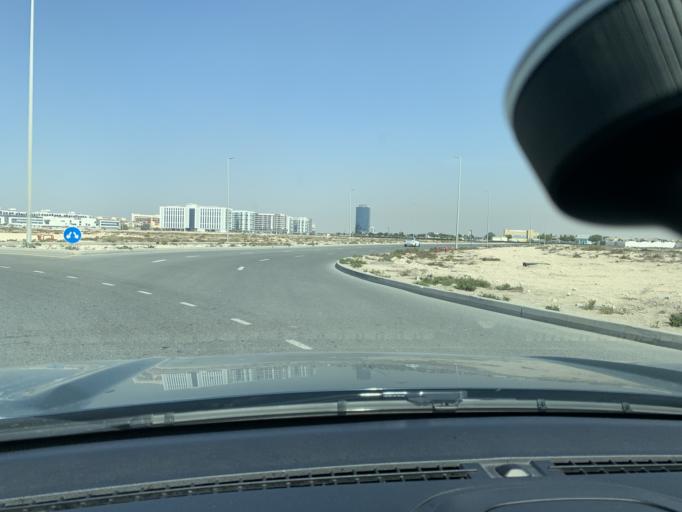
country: AE
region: Dubai
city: Dubai
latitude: 25.0344
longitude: 55.2405
